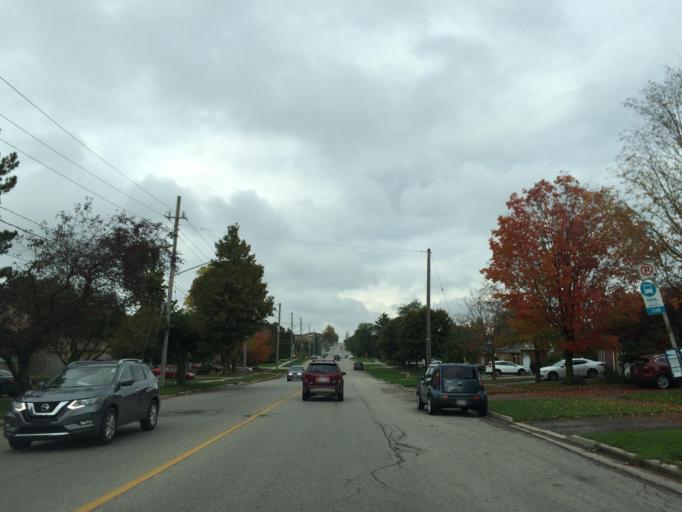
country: CA
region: Ontario
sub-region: Wellington County
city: Guelph
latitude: 43.5674
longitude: -80.2387
